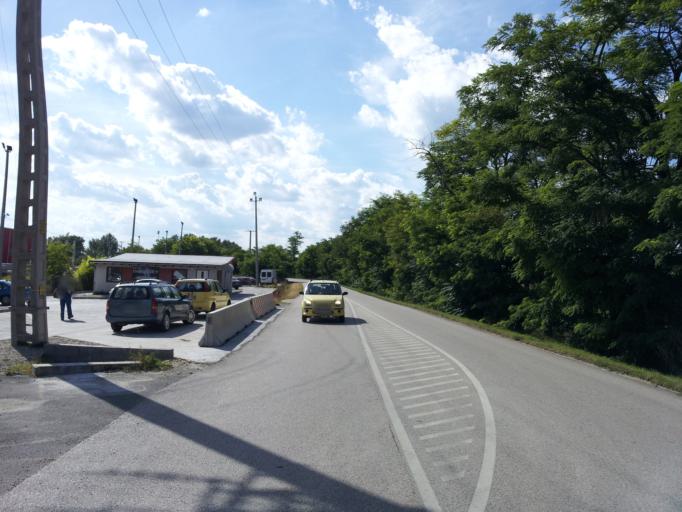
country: HU
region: Pest
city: Szigetcsep
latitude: 47.2626
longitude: 19.0099
